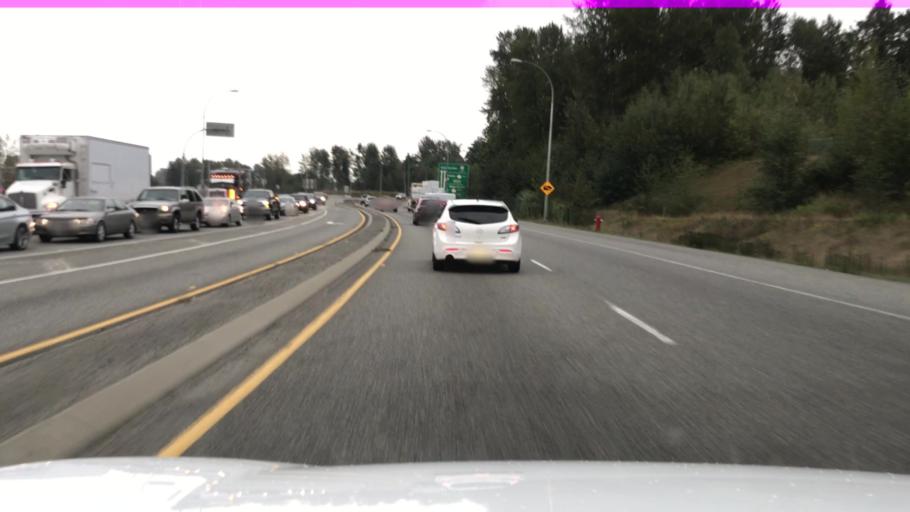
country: CA
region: British Columbia
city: Pitt Meadows
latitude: 49.1912
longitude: -122.7379
